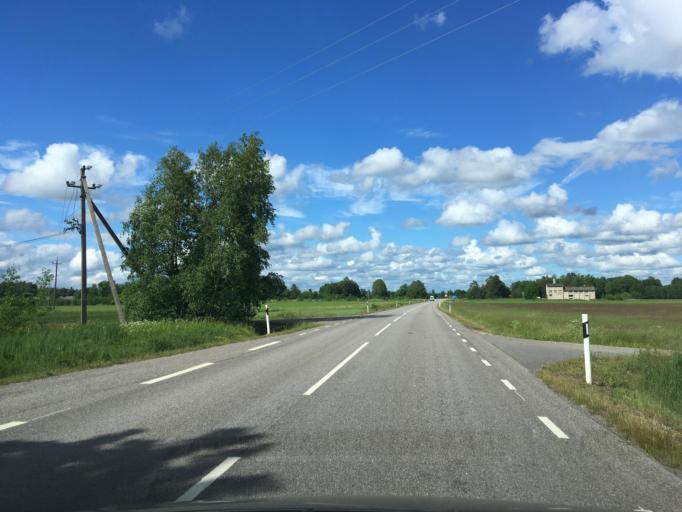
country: EE
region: Paernumaa
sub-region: Halinga vald
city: Parnu-Jaagupi
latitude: 58.6432
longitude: 24.5581
